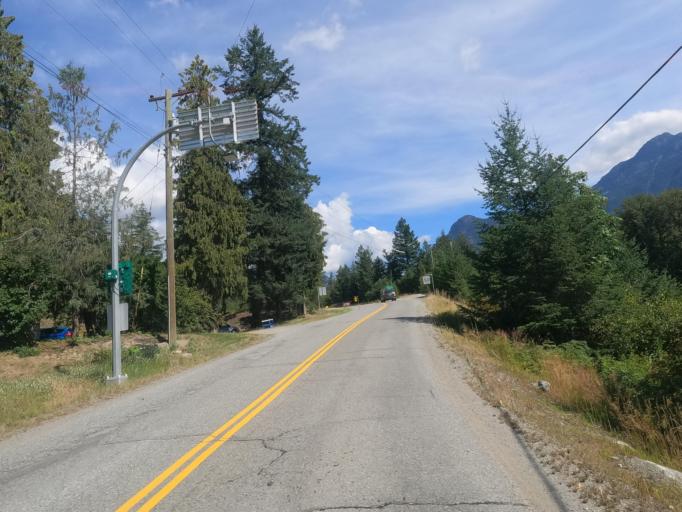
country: CA
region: British Columbia
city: Pemberton
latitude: 50.3209
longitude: -122.7209
